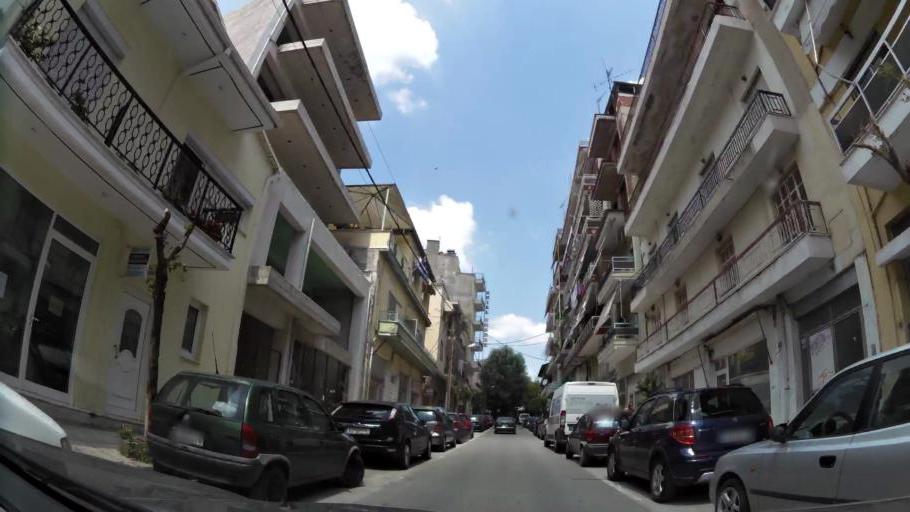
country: GR
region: West Macedonia
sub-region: Nomos Kozanis
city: Kozani
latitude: 40.2984
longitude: 21.7907
